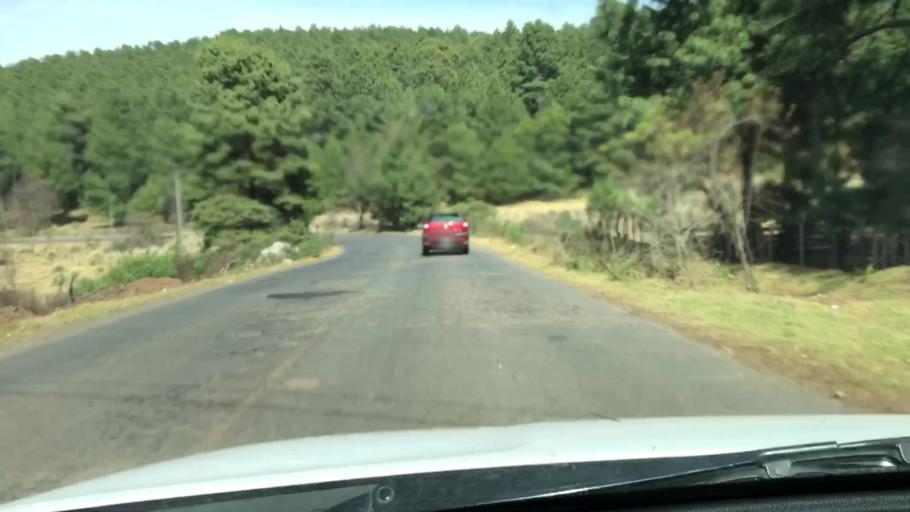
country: MX
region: Jalisco
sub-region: Amacueca
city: Tepec
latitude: 20.0505
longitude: -103.6965
